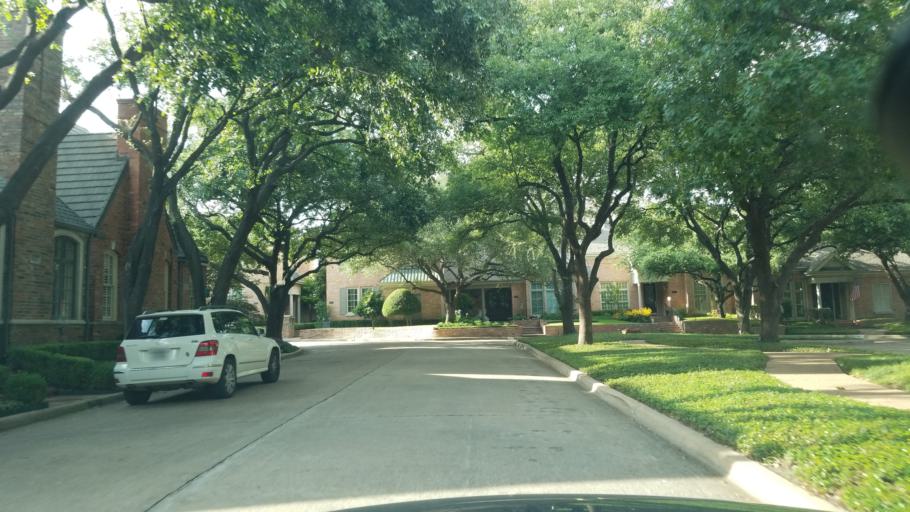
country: US
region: Texas
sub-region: Dallas County
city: University Park
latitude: 32.8591
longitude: -96.7722
